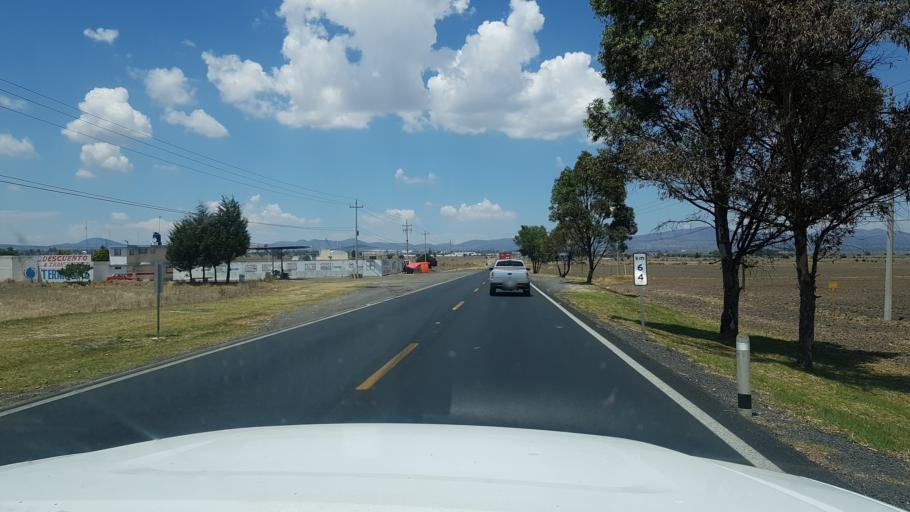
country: MX
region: Hidalgo
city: Calpulalpan
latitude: 19.5770
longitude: -98.5189
